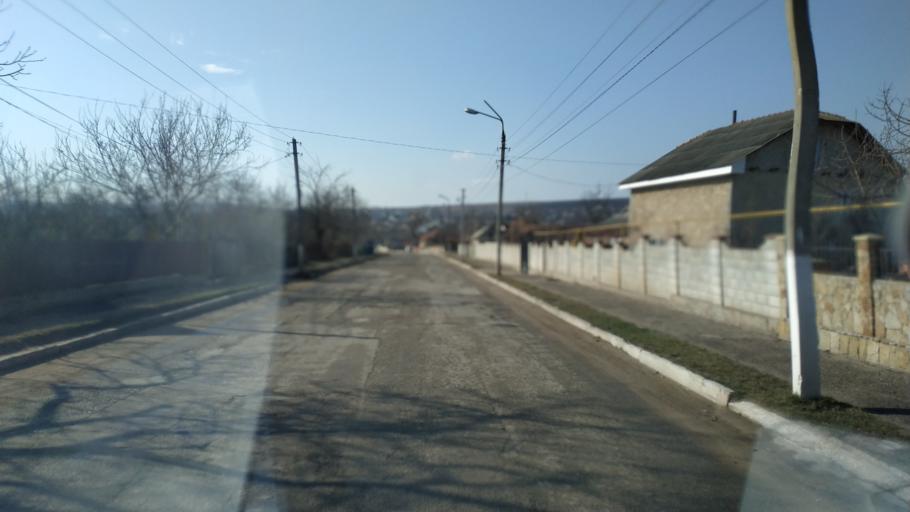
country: MD
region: Chisinau
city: Singera
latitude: 46.6841
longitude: 29.0488
